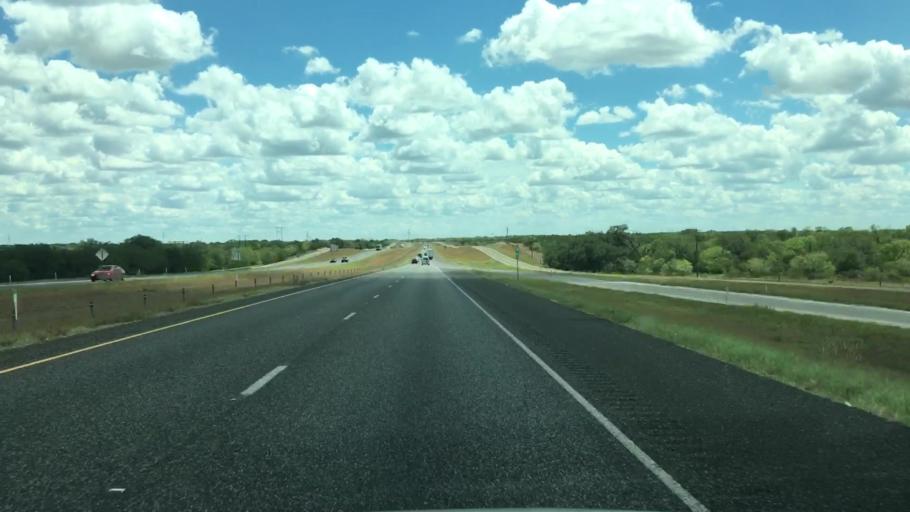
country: US
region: Texas
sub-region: Atascosa County
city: Pleasanton
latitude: 28.8421
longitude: -98.3763
